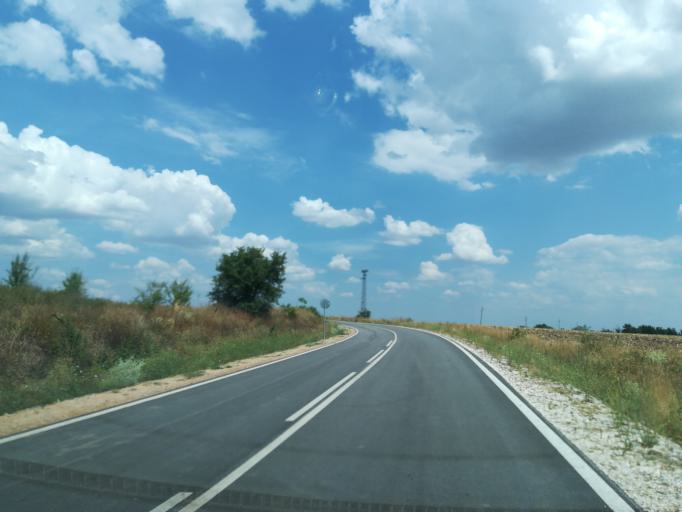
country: BG
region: Khaskovo
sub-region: Obshtina Mineralni Bani
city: Mineralni Bani
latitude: 41.9926
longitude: 25.1853
